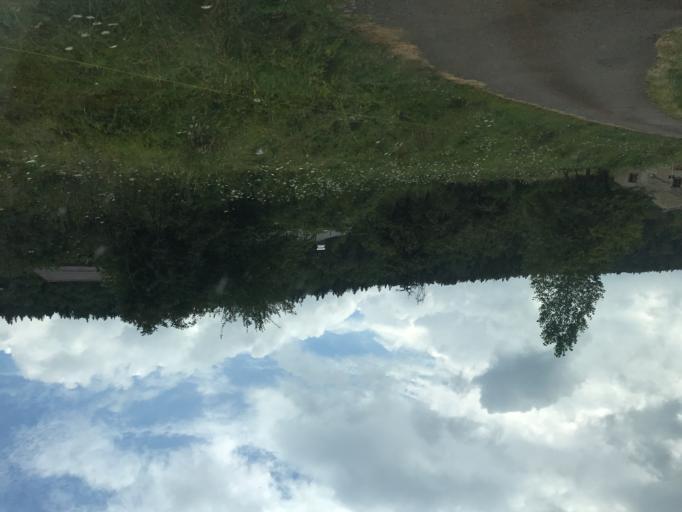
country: FR
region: Franche-Comte
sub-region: Departement du Jura
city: Longchaumois
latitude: 46.4755
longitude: 5.9004
